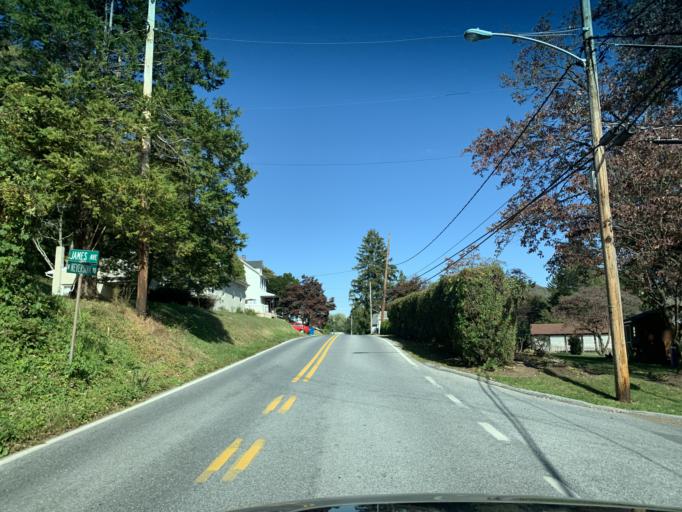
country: US
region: Pennsylvania
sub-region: Berks County
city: Reiffton
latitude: 40.3211
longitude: -75.8784
